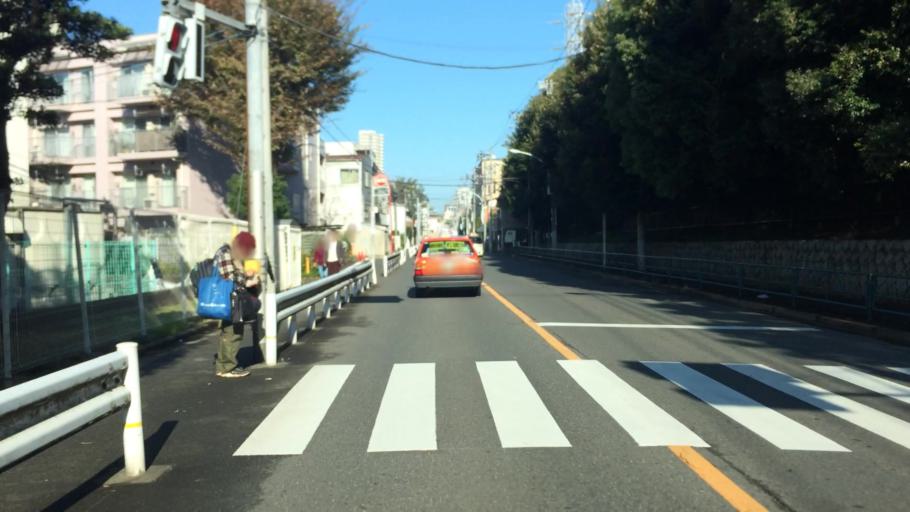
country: JP
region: Tokyo
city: Tokyo
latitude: 35.6273
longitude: 139.6645
